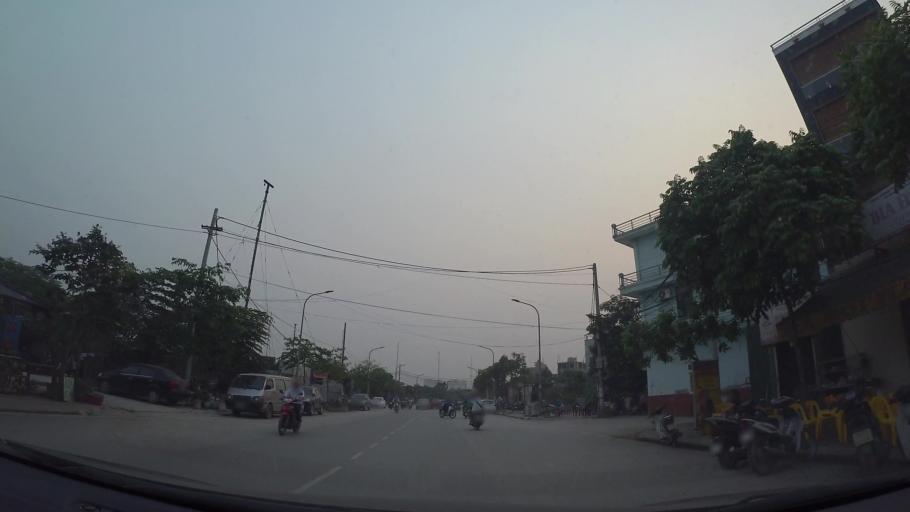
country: VN
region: Ha Noi
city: Thanh Xuan
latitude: 20.9782
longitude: 105.8061
